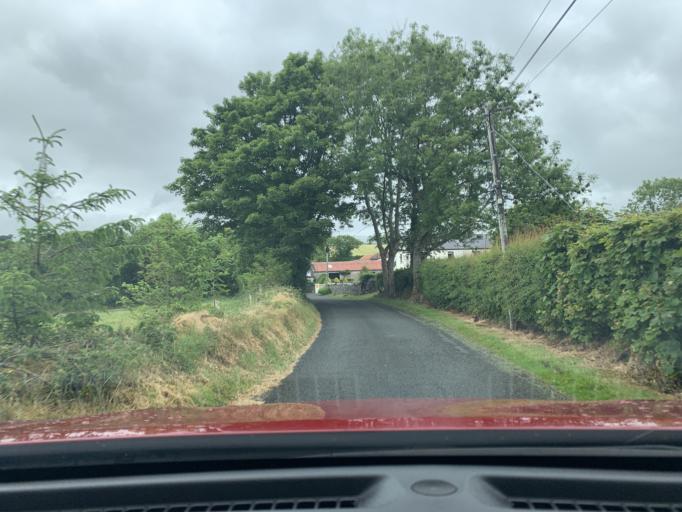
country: IE
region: Connaught
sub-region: Sligo
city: Sligo
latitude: 54.3014
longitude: -8.4576
